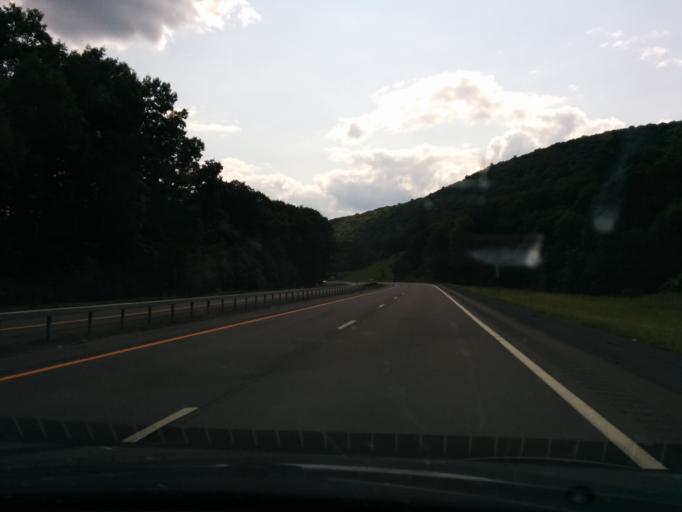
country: US
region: New York
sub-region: Delaware County
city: Hancock
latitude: 41.9683
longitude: -75.2261
